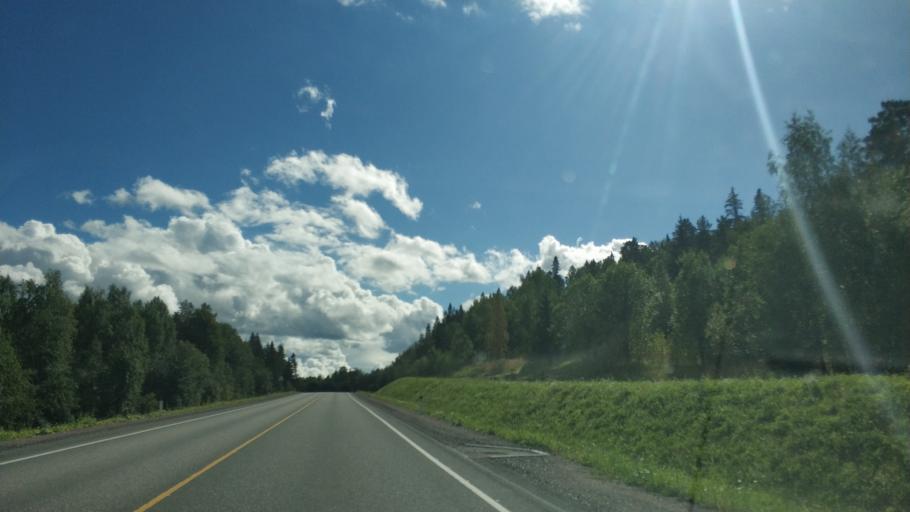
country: RU
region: Republic of Karelia
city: Ruskeala
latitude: 61.9005
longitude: 30.6354
